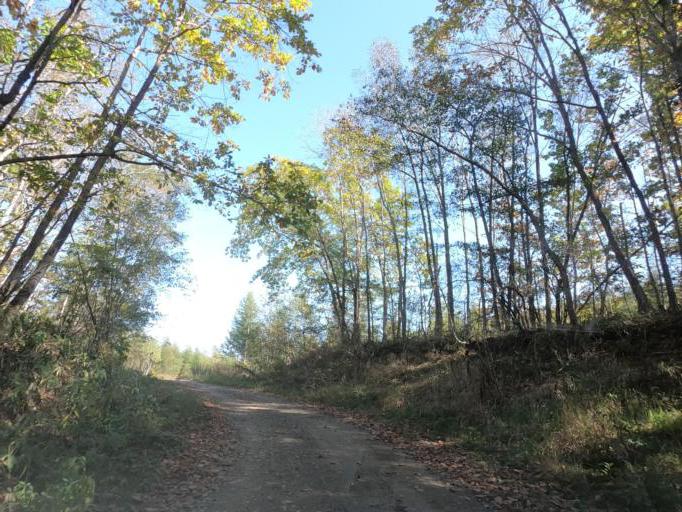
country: JP
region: Hokkaido
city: Obihiro
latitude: 42.7275
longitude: 143.4509
